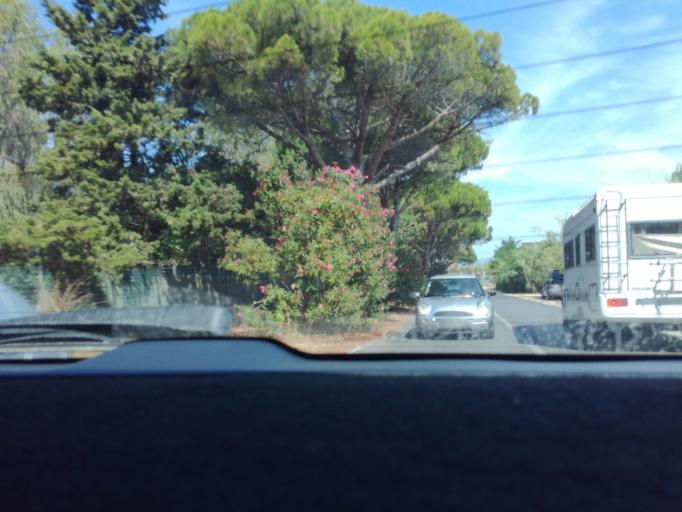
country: FR
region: Provence-Alpes-Cote d'Azur
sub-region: Departement du Var
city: Hyeres
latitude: 43.0390
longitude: 6.1449
